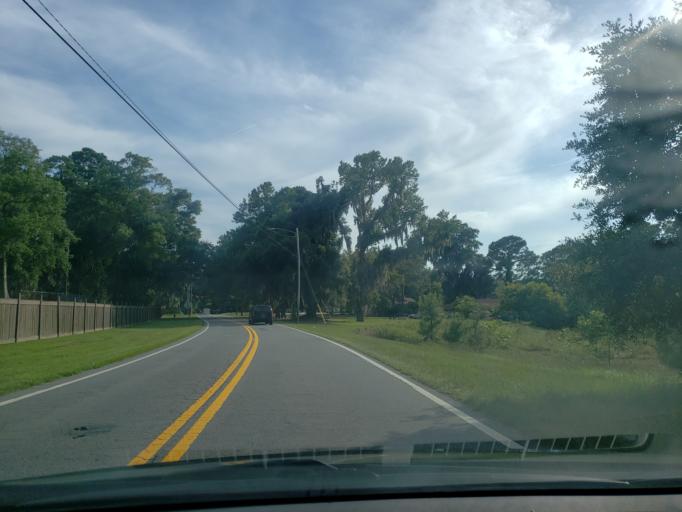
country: US
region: Georgia
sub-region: Chatham County
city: Montgomery
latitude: 31.9578
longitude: -81.1423
